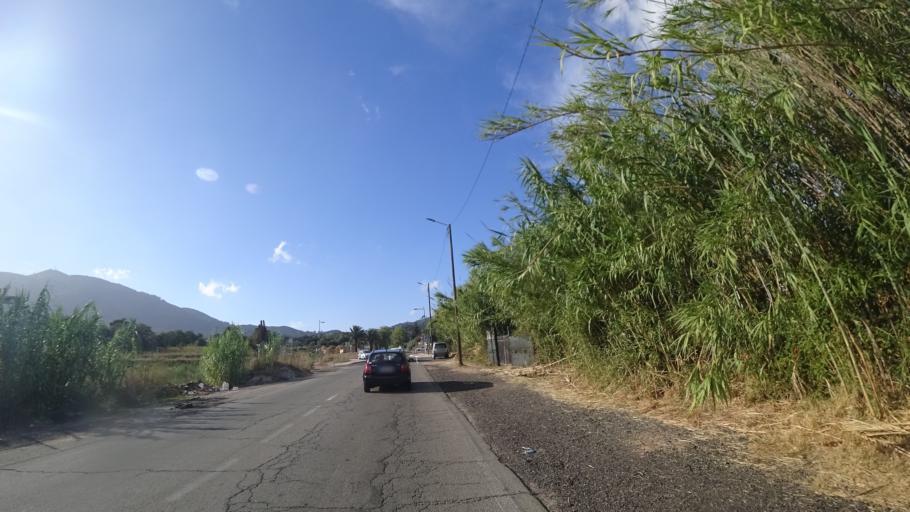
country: FR
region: Corsica
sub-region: Departement de la Corse-du-Sud
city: Ajaccio
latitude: 41.9379
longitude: 8.7423
